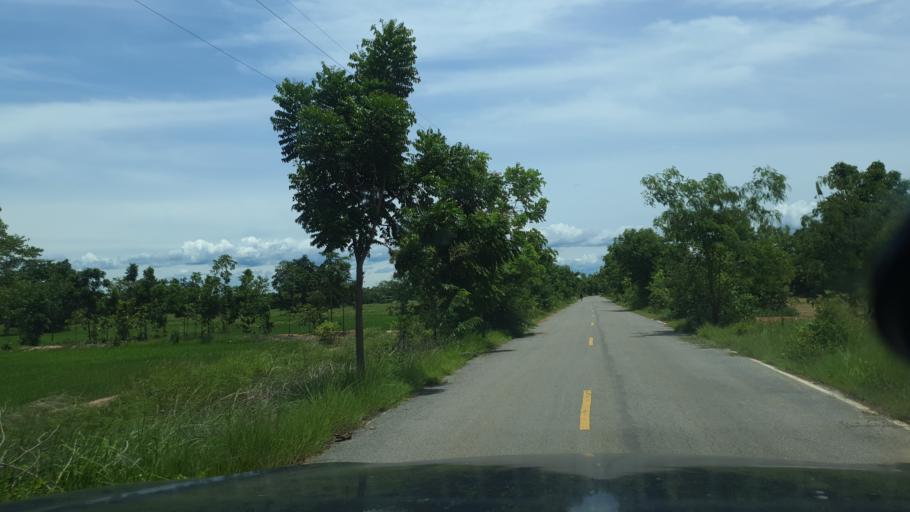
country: TH
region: Sukhothai
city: Ban Na
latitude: 17.1230
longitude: 99.6740
